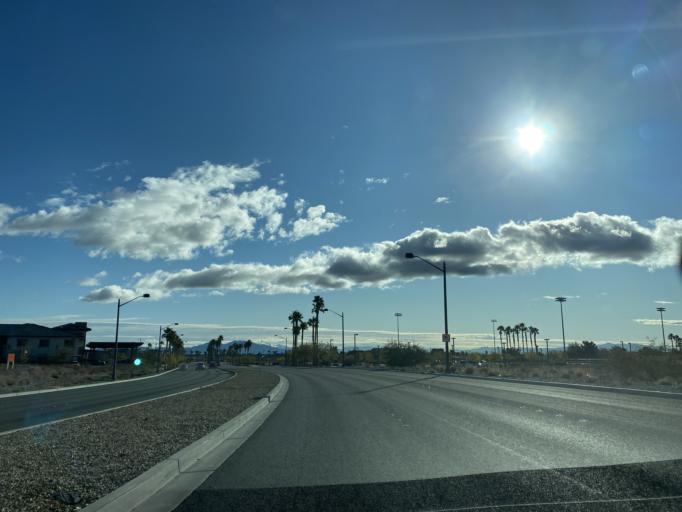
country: US
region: Nevada
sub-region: Clark County
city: Summerlin South
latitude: 36.2745
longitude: -115.2859
